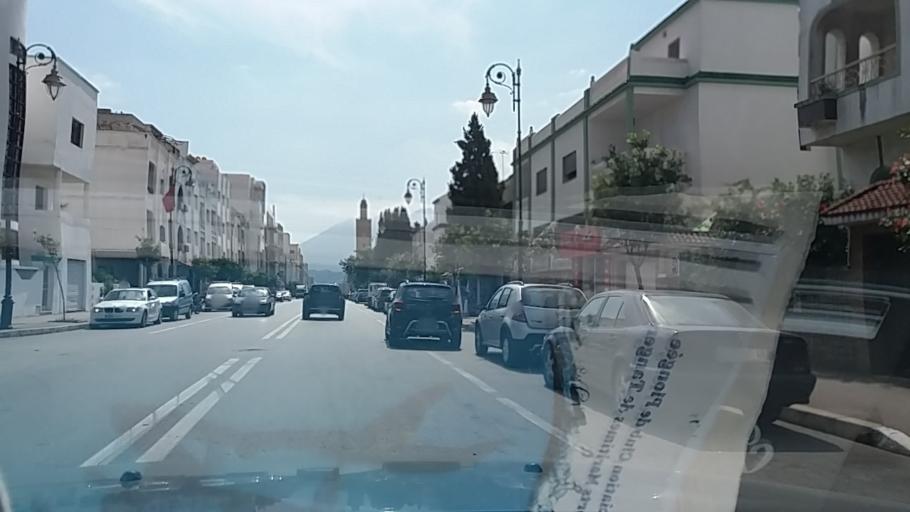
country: MA
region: Tanger-Tetouan
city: Tetouan
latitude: 35.5835
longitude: -5.3458
